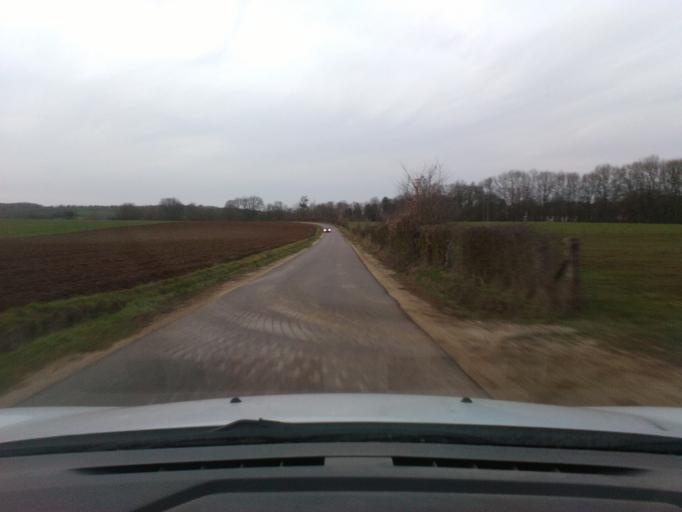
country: FR
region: Lorraine
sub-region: Departement des Vosges
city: Mirecourt
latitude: 48.2860
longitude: 6.1148
